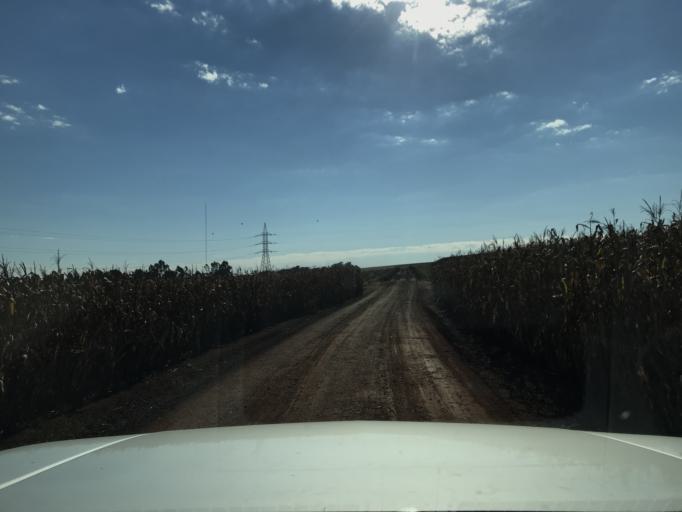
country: BR
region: Parana
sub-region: Palotina
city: Palotina
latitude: -24.2741
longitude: -53.8188
